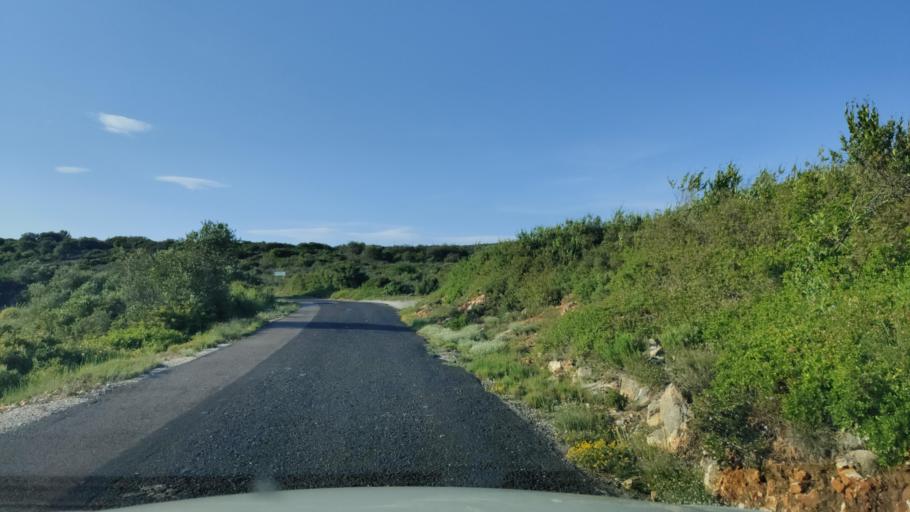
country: FR
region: Languedoc-Roussillon
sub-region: Departement des Pyrenees-Orientales
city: Estagel
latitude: 42.7873
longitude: 2.7442
